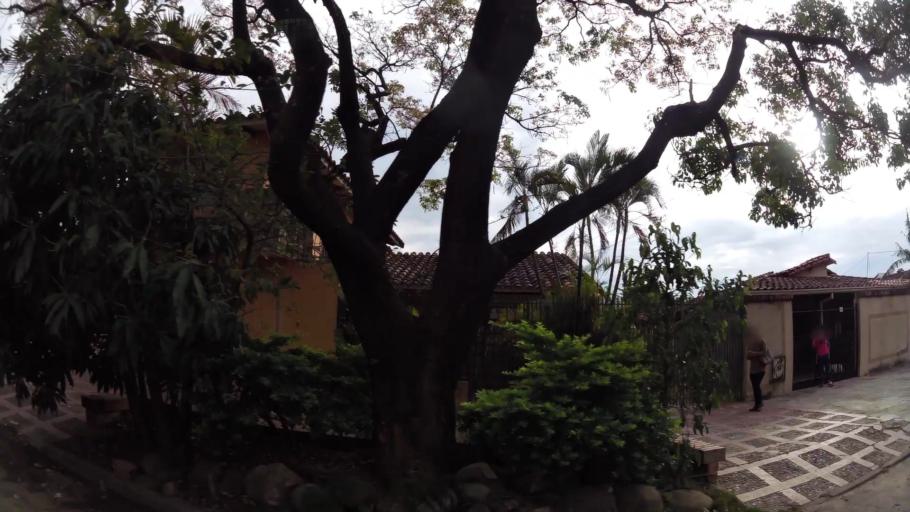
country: BO
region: Santa Cruz
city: Santa Cruz de la Sierra
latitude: -17.7524
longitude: -63.1678
